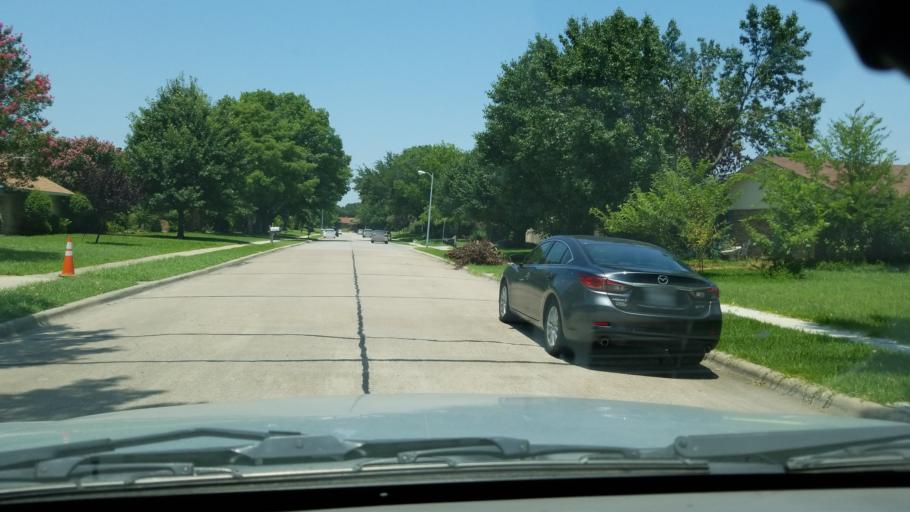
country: US
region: Texas
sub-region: Dallas County
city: Coppell
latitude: 32.9646
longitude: -96.9910
